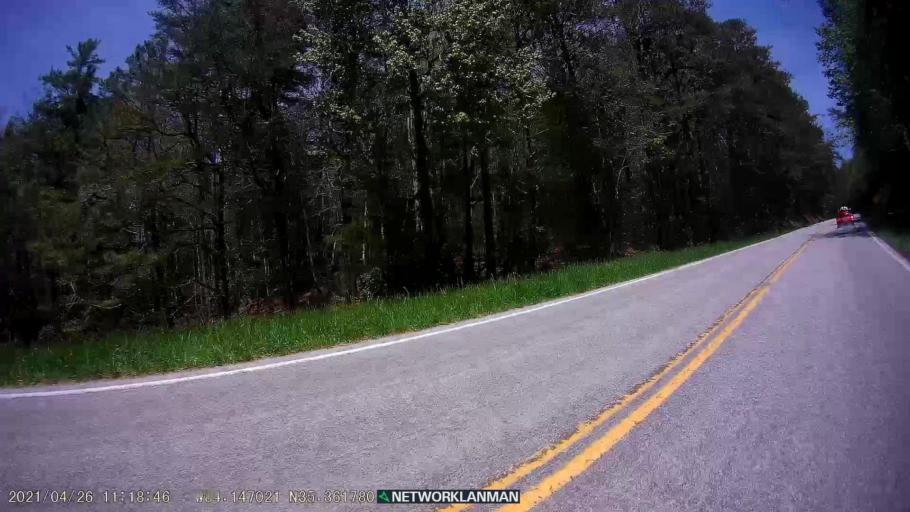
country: US
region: Tennessee
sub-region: Monroe County
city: Vonore
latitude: 35.3619
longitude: -84.1470
